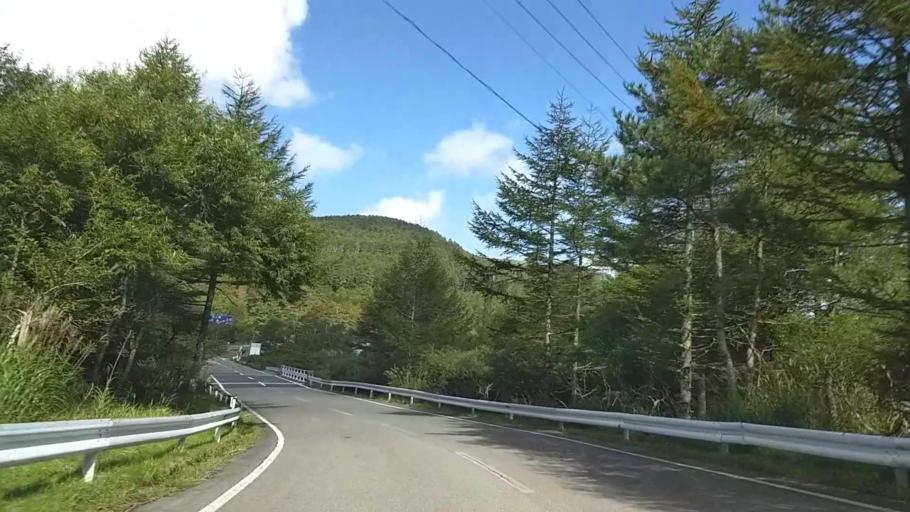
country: JP
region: Nagano
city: Suwa
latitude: 36.1462
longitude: 138.1446
